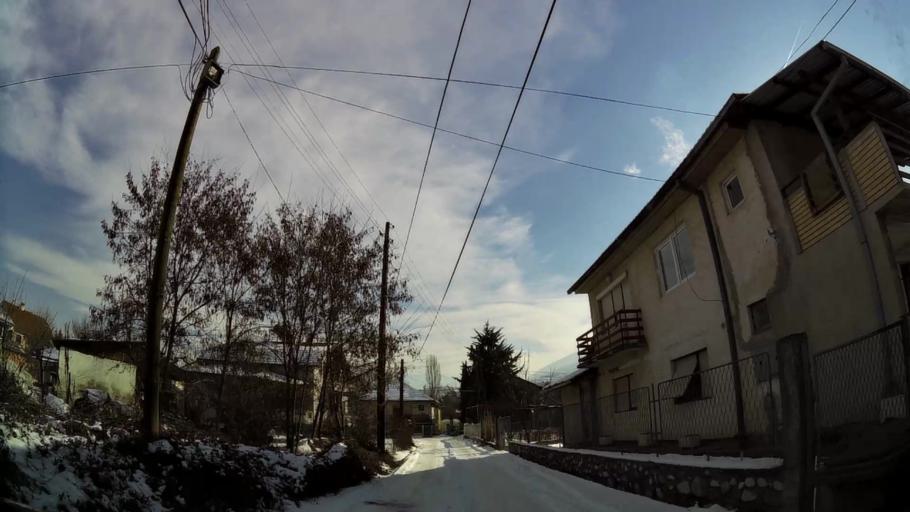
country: MK
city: Krushopek
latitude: 41.9987
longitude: 21.3711
